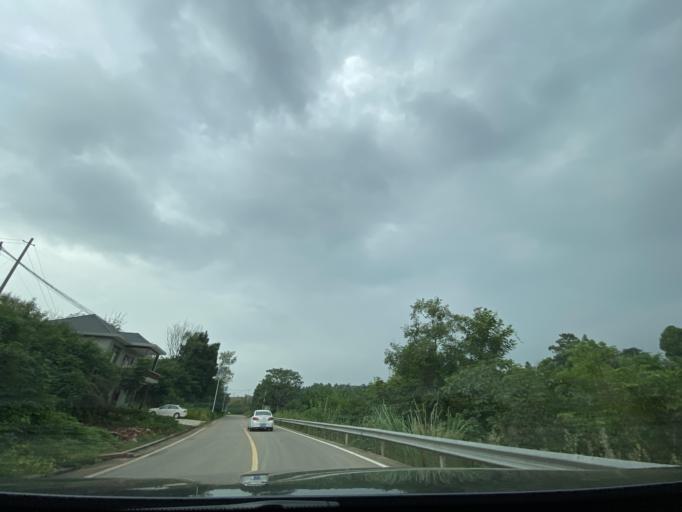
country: CN
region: Sichuan
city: Jiancheng
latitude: 30.5490
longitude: 104.5236
